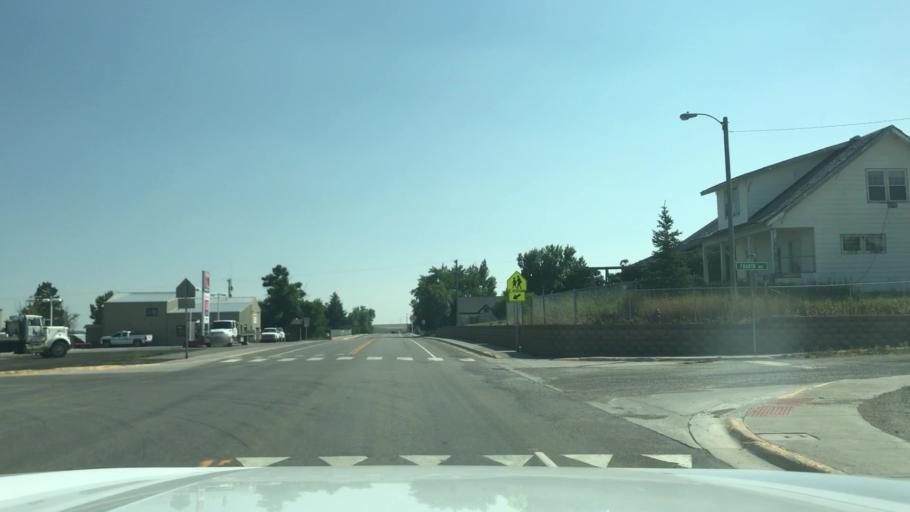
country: US
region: Montana
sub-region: Wheatland County
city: Harlowton
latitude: 46.6793
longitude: -109.7524
